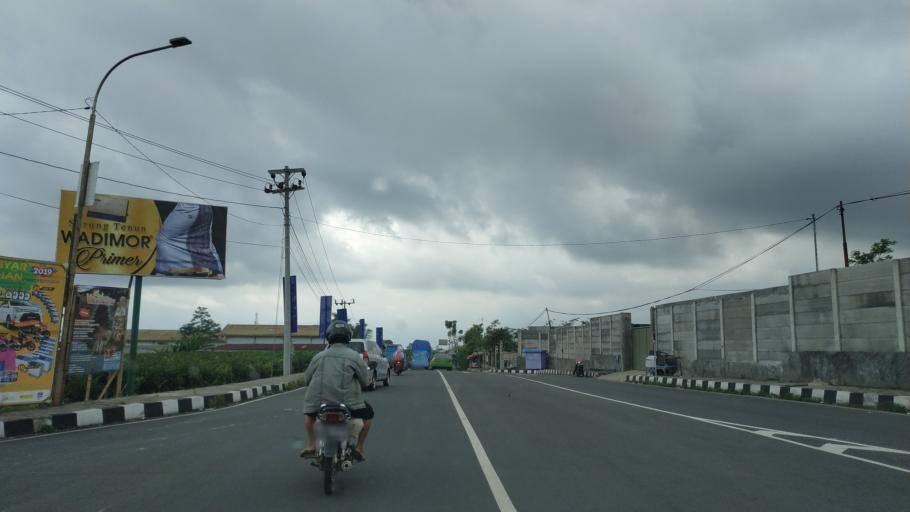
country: ID
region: Central Java
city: Magelang
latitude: -7.2845
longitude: 110.1101
